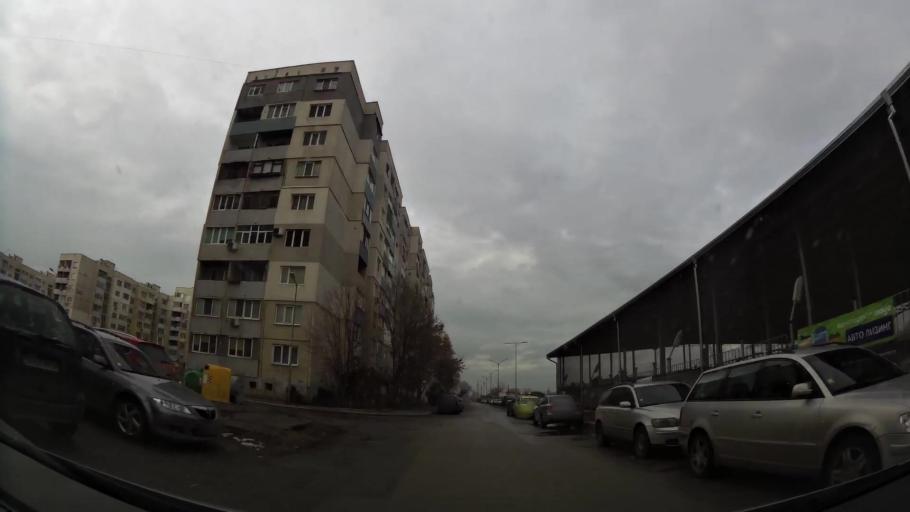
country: BG
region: Sofia-Capital
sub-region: Stolichna Obshtina
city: Sofia
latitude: 42.7447
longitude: 23.2821
